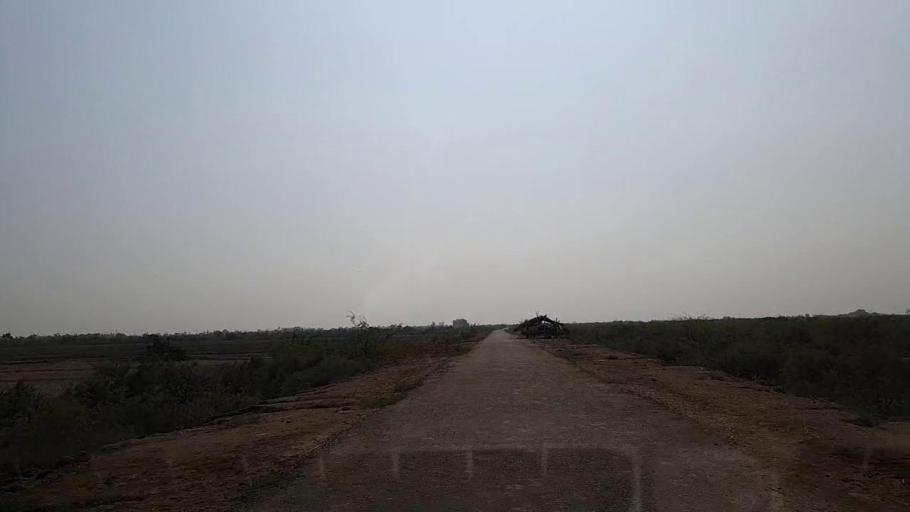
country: PK
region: Sindh
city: Mirpur Sakro
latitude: 24.6580
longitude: 67.6922
